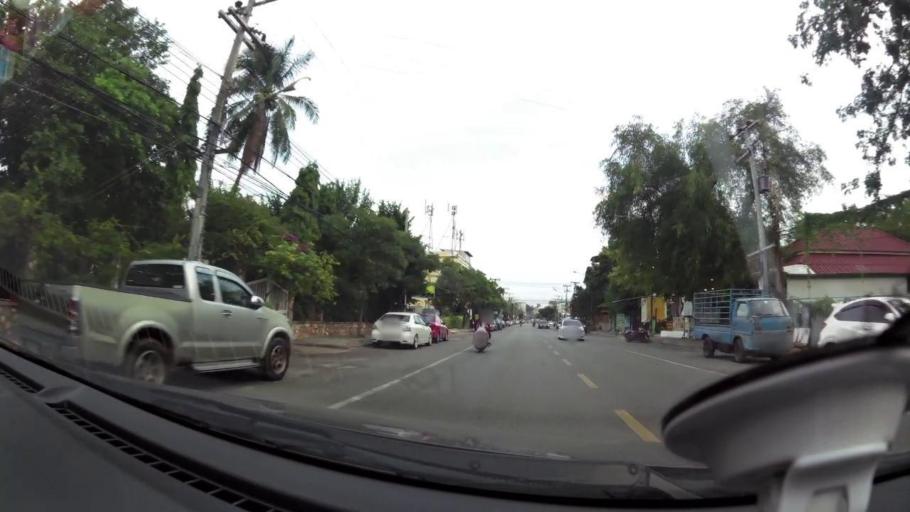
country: TH
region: Prachuap Khiri Khan
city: Hua Hin
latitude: 12.5802
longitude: 99.9559
